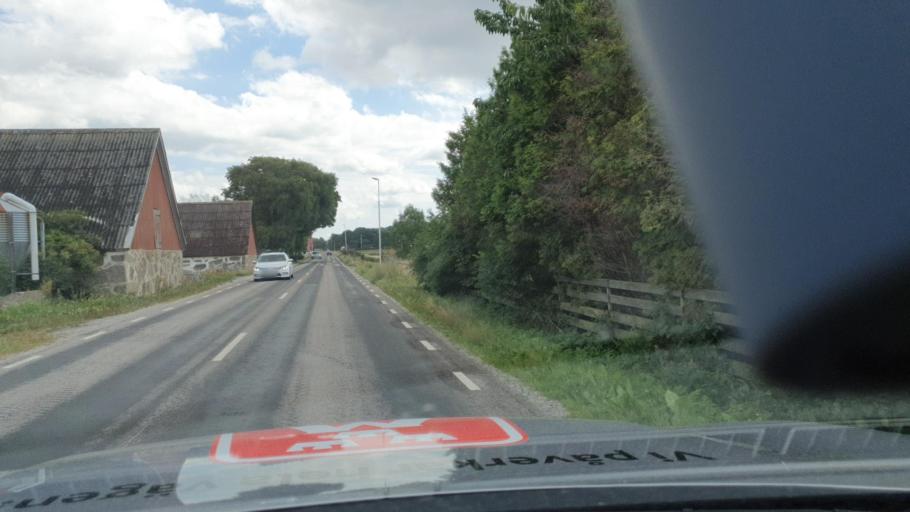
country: SE
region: Blekinge
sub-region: Solvesborgs Kommun
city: Soelvesborg
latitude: 56.0401
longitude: 14.6979
